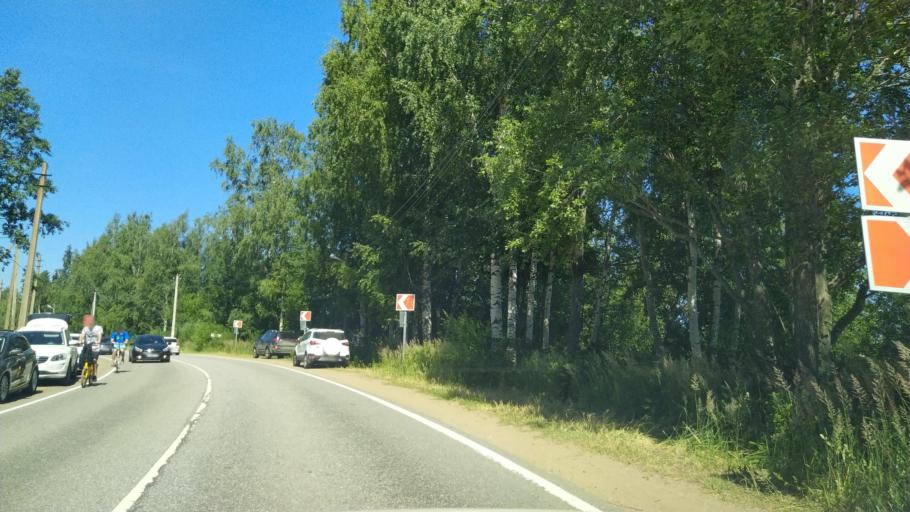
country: RU
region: Leningrad
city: Borisova Griva
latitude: 60.1147
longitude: 31.0834
